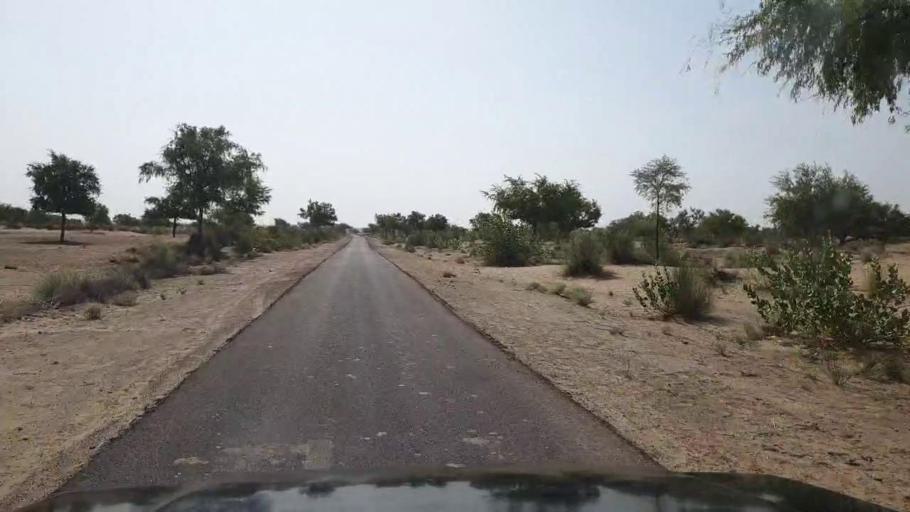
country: PK
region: Sindh
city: Islamkot
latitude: 24.9381
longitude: 70.0873
